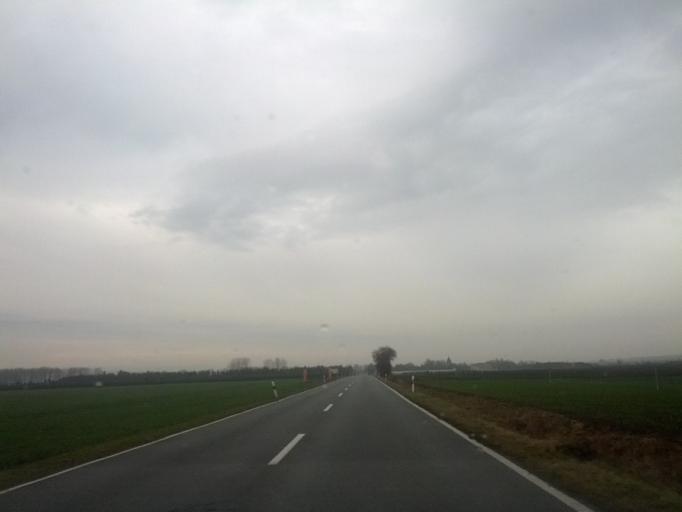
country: DE
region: Thuringia
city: Zimmernsupra
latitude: 50.9694
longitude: 10.9000
